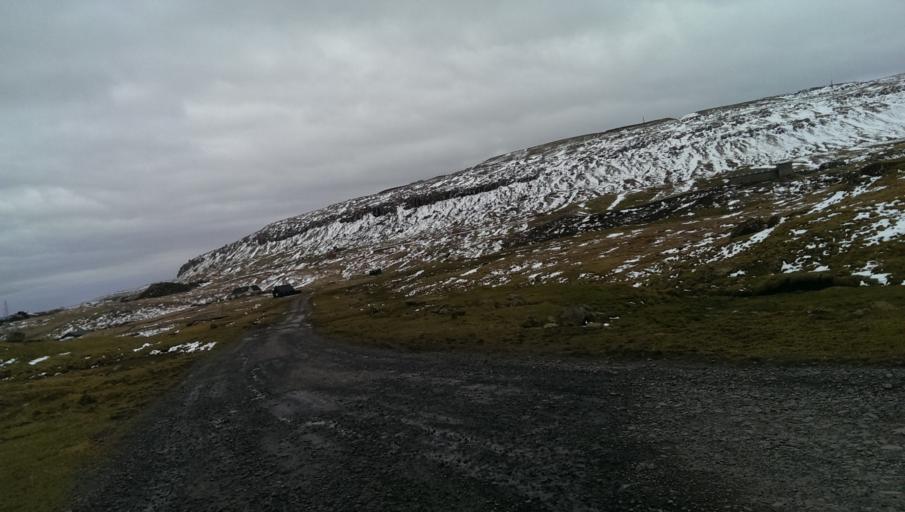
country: FO
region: Streymoy
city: Hoyvik
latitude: 62.0345
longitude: -6.7998
